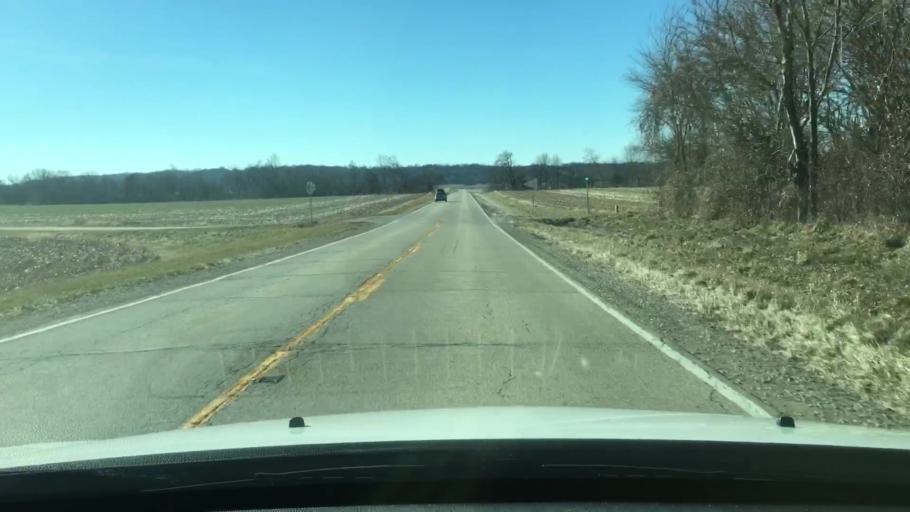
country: US
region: Illinois
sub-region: Mason County
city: Havana
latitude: 40.2847
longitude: -90.1620
